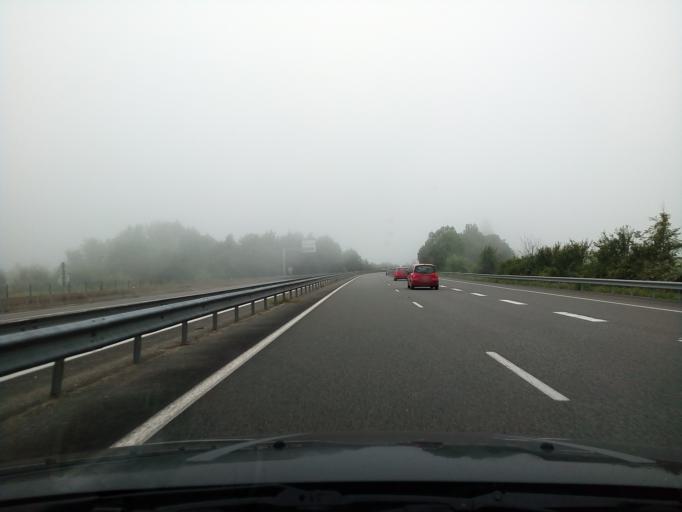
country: FR
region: Poitou-Charentes
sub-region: Departement de la Charente
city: Jarnac
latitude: 45.6902
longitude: -0.1371
